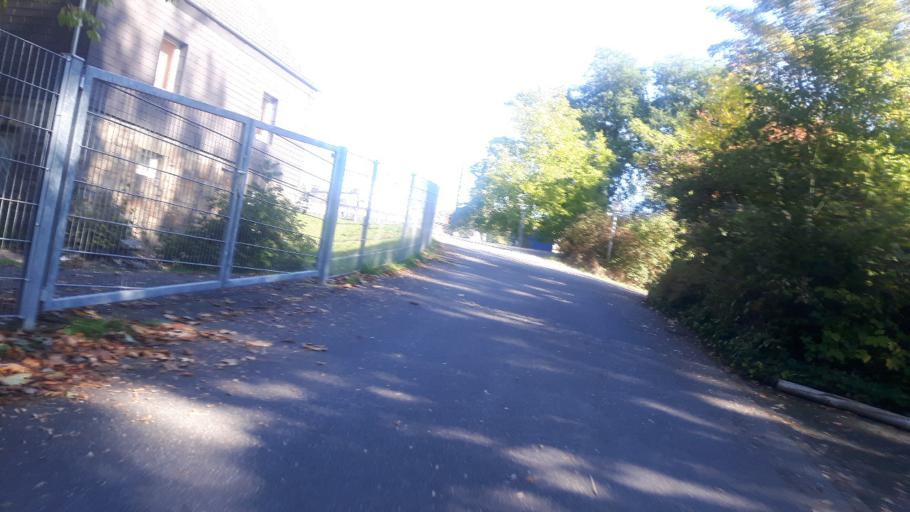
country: DE
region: Rheinland-Pfalz
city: Niederirsen
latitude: 50.7962
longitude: 7.6083
